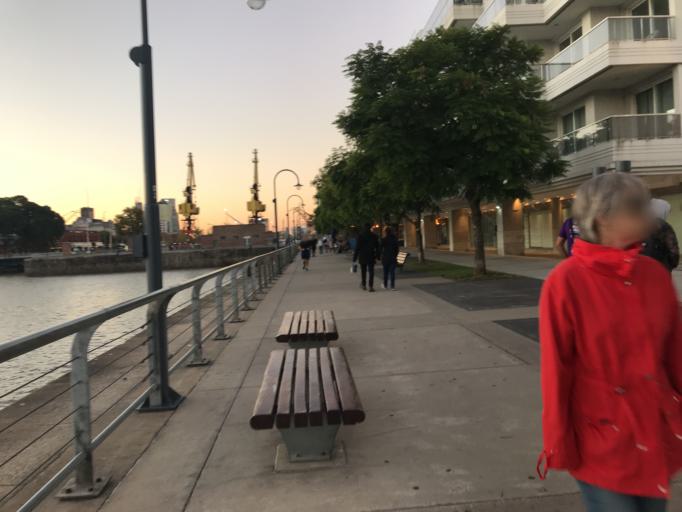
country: AR
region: Buenos Aires F.D.
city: Buenos Aires
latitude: -34.6136
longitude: -58.3635
